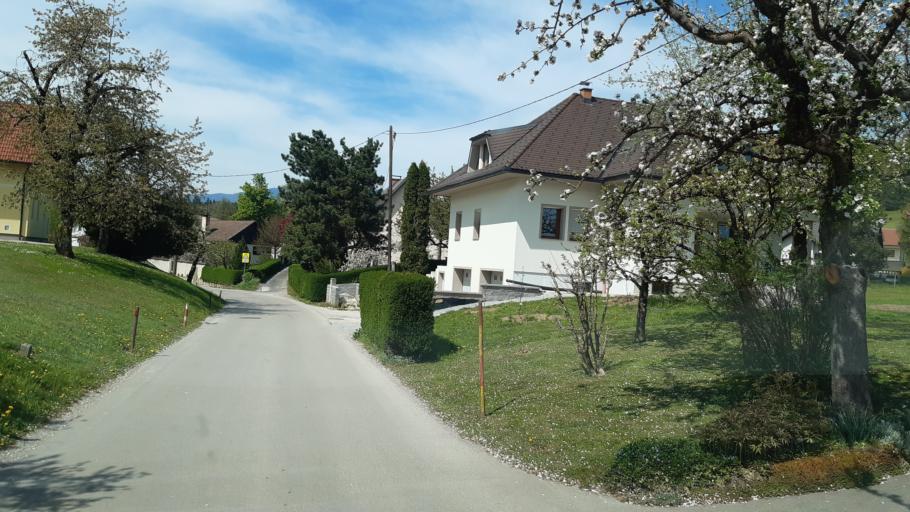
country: SI
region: Domzale
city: Radomlje
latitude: 46.1791
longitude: 14.6332
